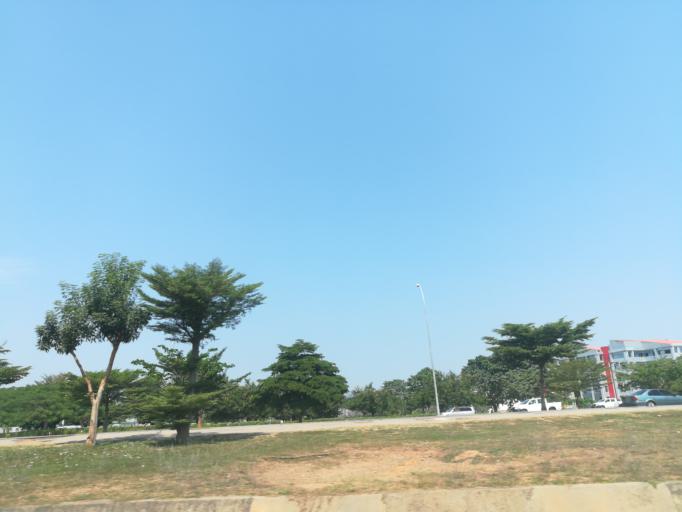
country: NG
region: Abuja Federal Capital Territory
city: Abuja
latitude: 9.0769
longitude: 7.4336
